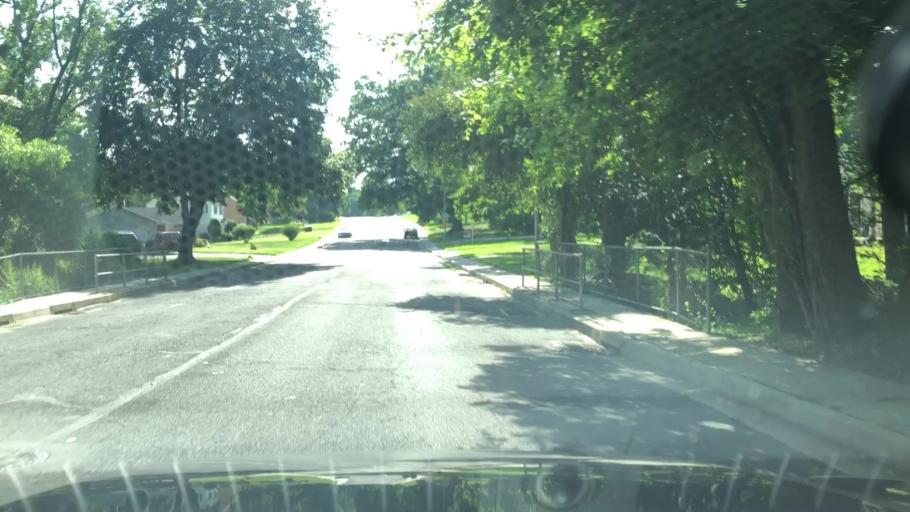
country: US
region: Pennsylvania
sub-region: Bucks County
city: Fairless Hills
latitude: 40.1832
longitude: -74.8464
